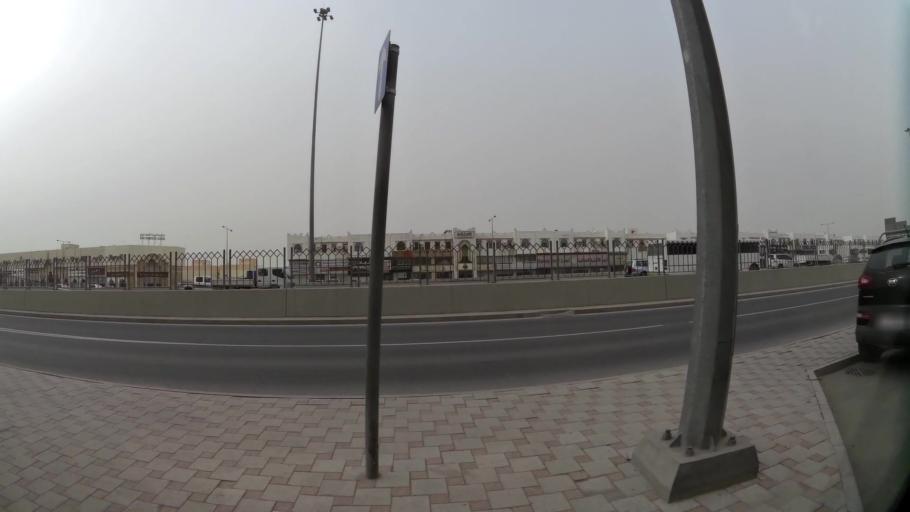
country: QA
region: Baladiyat ad Dawhah
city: Doha
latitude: 25.2590
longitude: 51.4893
